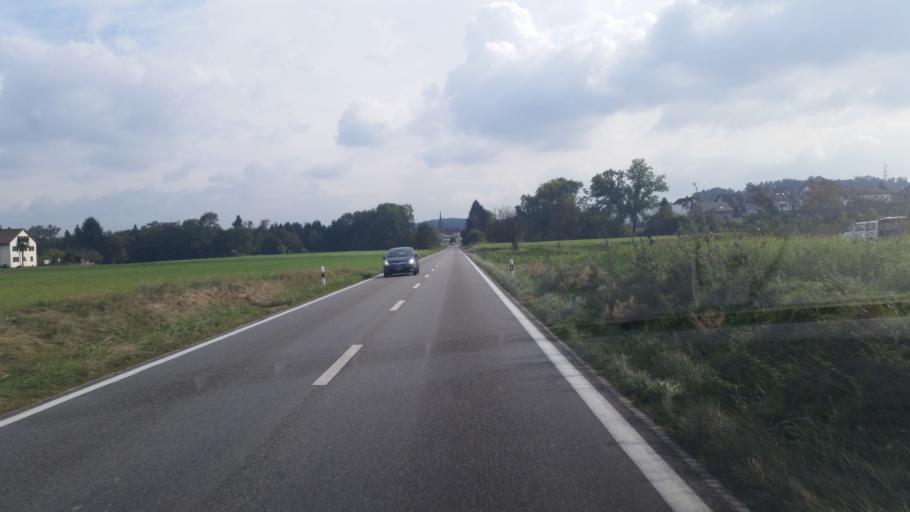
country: CH
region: Aargau
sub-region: Bezirk Baden
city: Kunten
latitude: 47.3815
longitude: 8.2997
